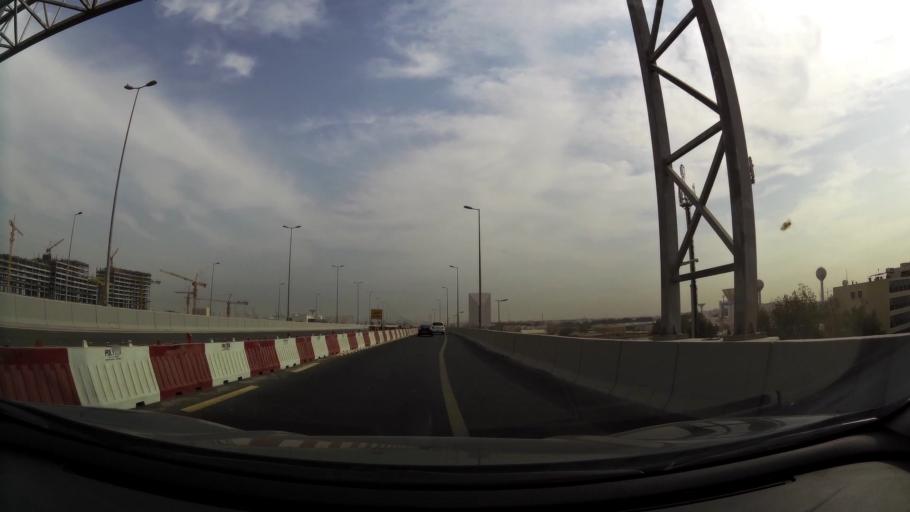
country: KW
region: Al Asimah
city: Ar Rabiyah
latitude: 29.3286
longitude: 47.9018
